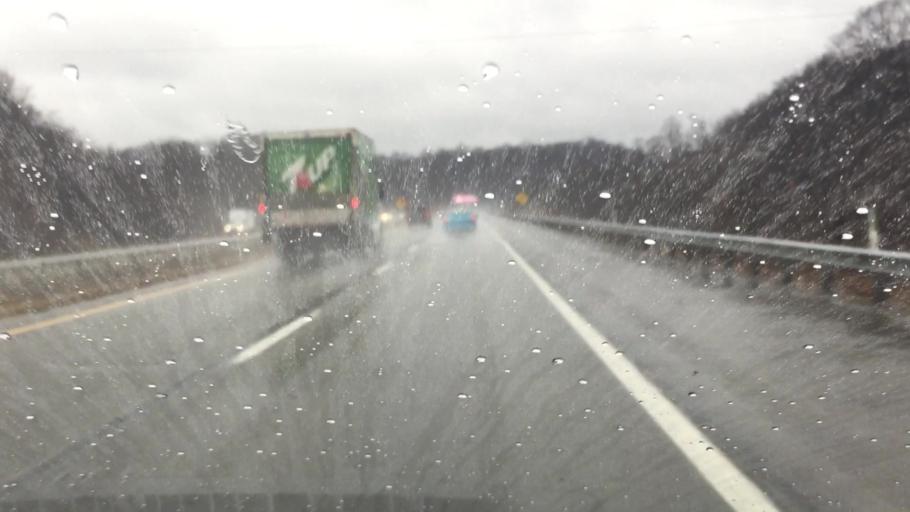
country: US
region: Pennsylvania
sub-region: Allegheny County
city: Franklin Park
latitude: 40.5466
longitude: -80.0841
